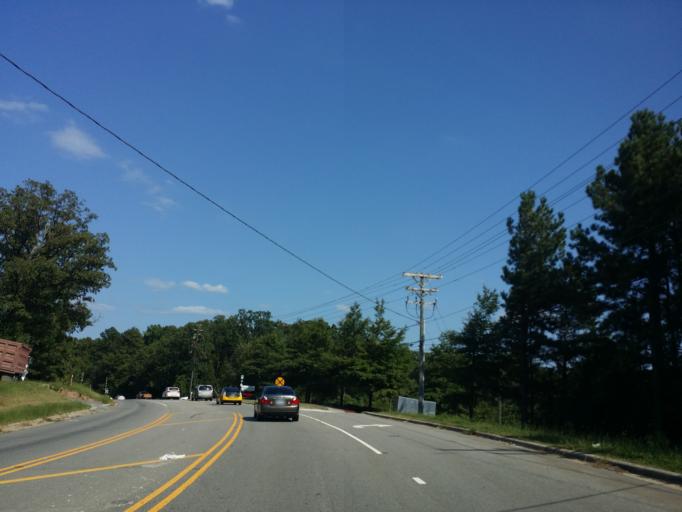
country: US
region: North Carolina
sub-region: Durham County
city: Durham
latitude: 35.9383
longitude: -78.8517
